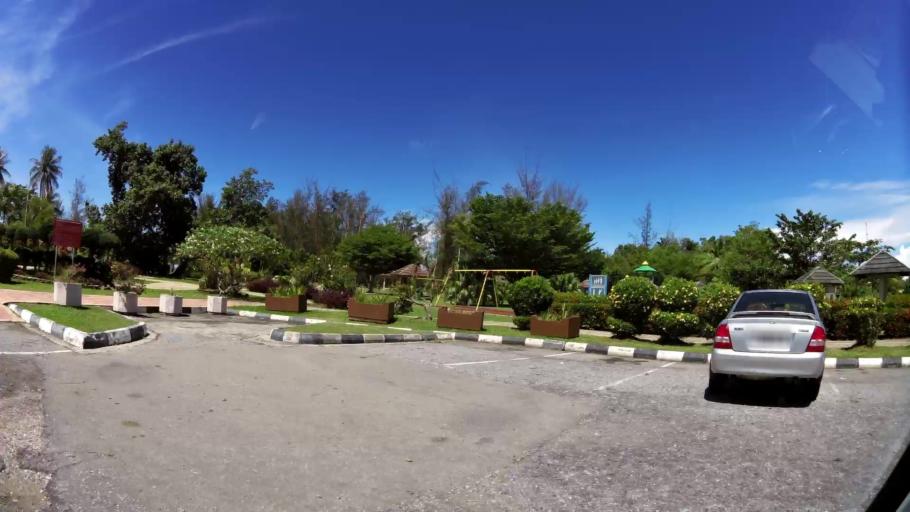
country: BN
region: Brunei and Muara
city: Bandar Seri Begawan
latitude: 5.0365
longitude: 115.0795
